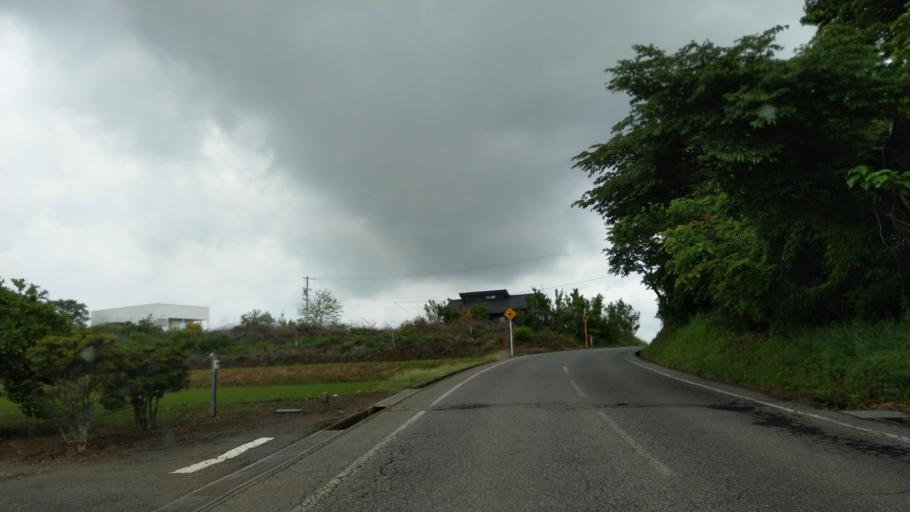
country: JP
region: Nagano
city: Komoro
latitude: 36.2969
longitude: 138.3850
